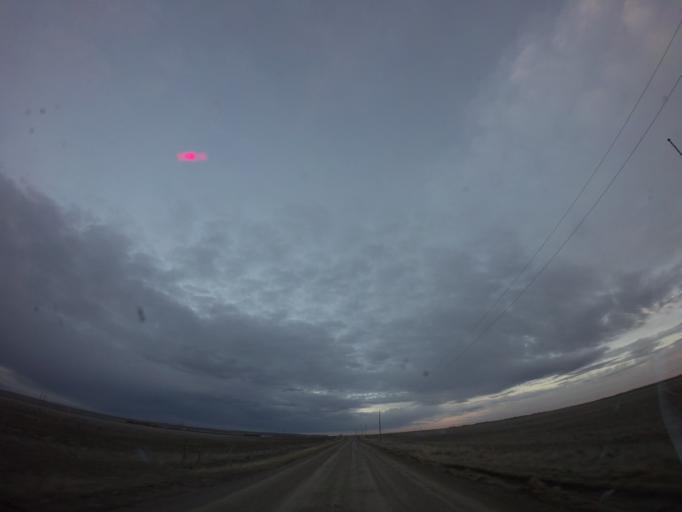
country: US
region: Montana
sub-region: Yellowstone County
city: Billings
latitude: 45.9436
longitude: -108.7238
